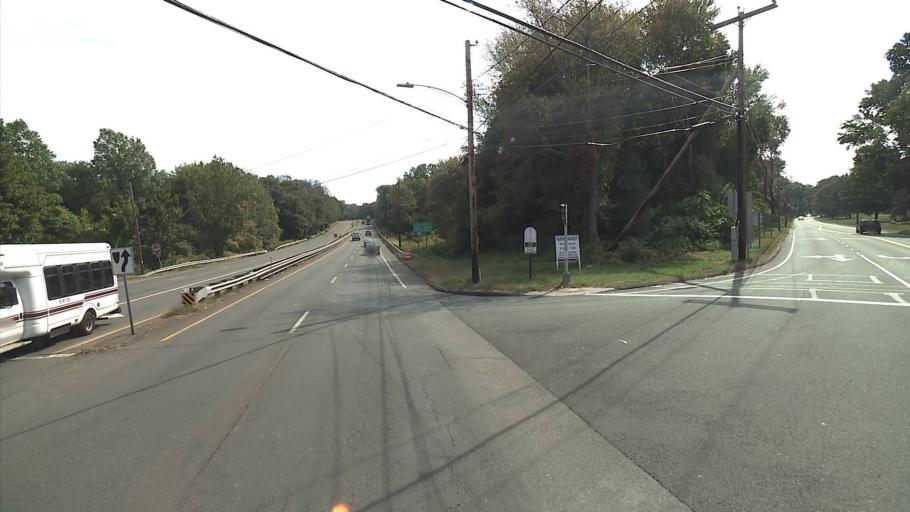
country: US
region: Connecticut
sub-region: New Haven County
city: Orange
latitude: 41.3020
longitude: -73.0263
